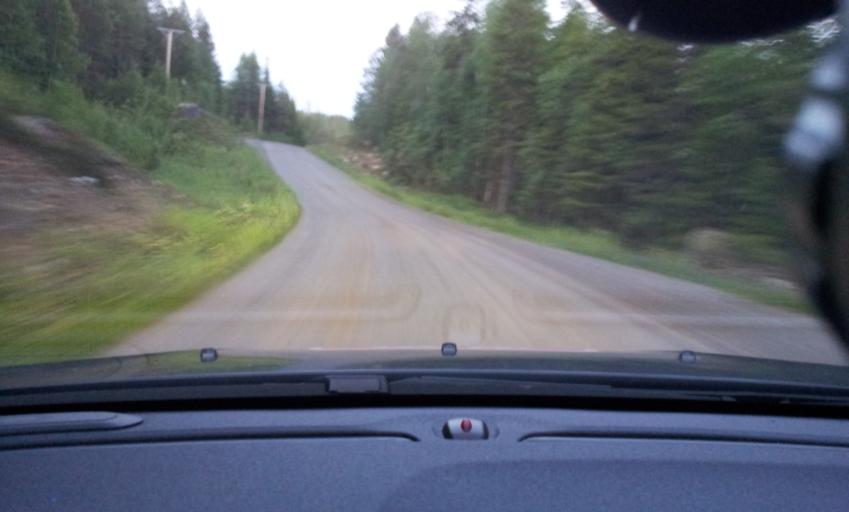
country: SE
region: Vaesternorrland
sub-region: Ange Kommun
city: Fransta
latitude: 62.8260
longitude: 16.0003
